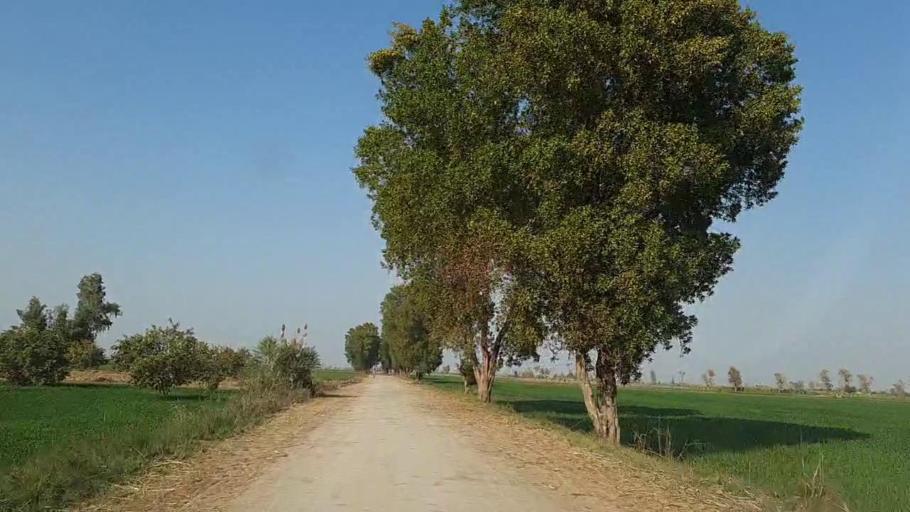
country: PK
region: Sindh
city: Daur
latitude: 26.4823
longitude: 68.2973
